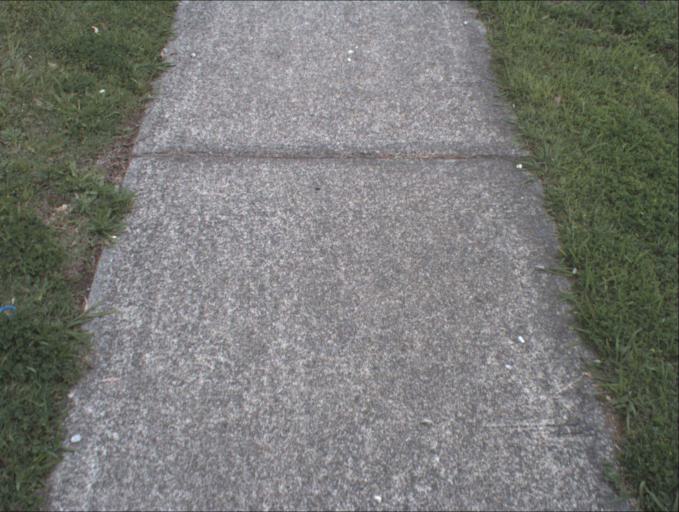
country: AU
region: Queensland
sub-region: Logan
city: Waterford West
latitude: -27.6907
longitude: 153.1508
